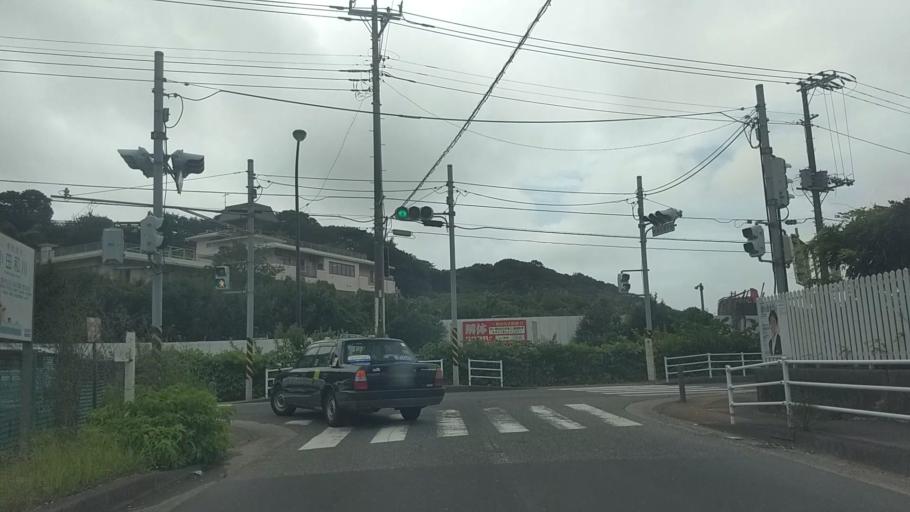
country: JP
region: Kanagawa
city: Yokosuka
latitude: 35.2318
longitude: 139.6454
